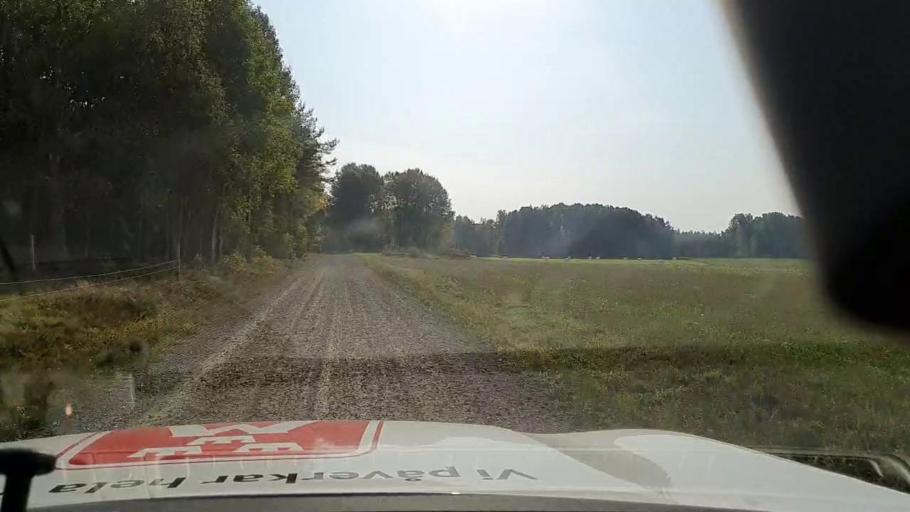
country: SE
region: Vaestmanland
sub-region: Kungsors Kommun
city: Kungsoer
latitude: 59.3507
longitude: 16.1643
